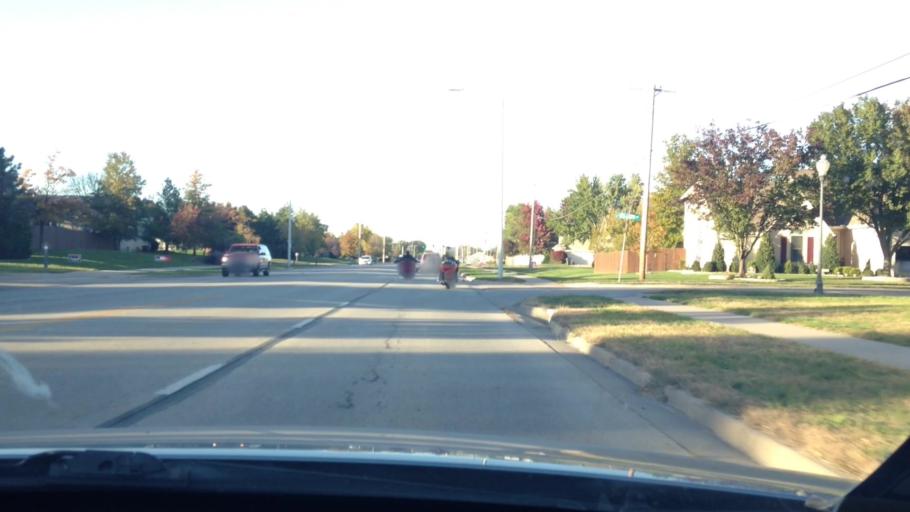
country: US
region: Kansas
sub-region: Johnson County
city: Gardner
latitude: 38.8193
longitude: -94.9276
